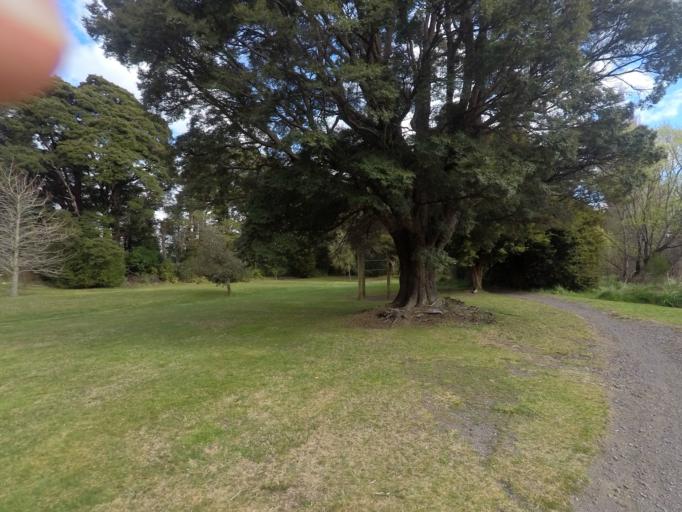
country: NZ
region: Manawatu-Wanganui
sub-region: Ruapehu District
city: Waiouru
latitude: -39.4126
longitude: 175.4002
